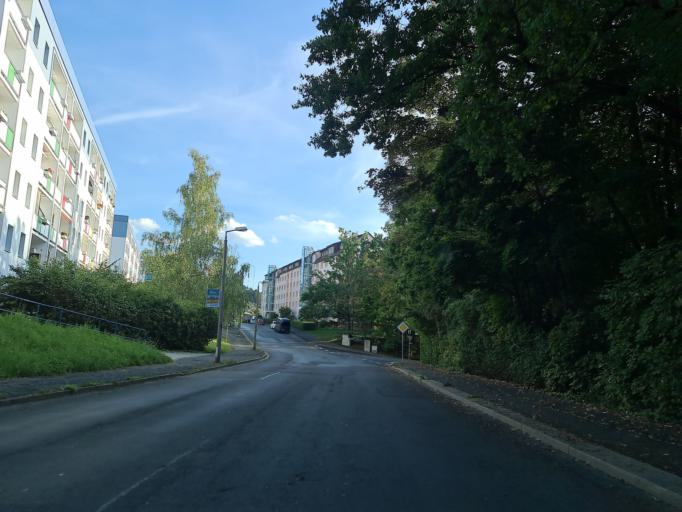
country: DE
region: Saxony
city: Plauen
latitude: 50.4871
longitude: 12.1422
